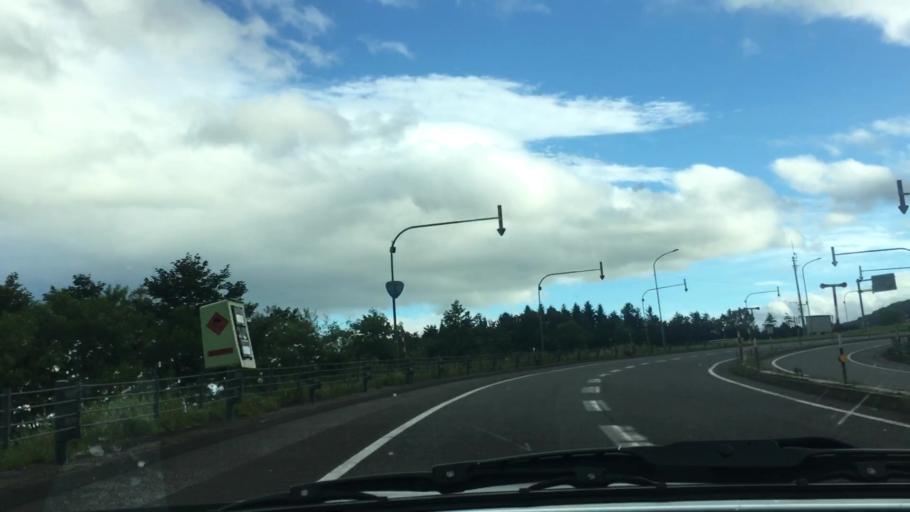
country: JP
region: Hokkaido
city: Otofuke
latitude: 43.1623
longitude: 142.8040
